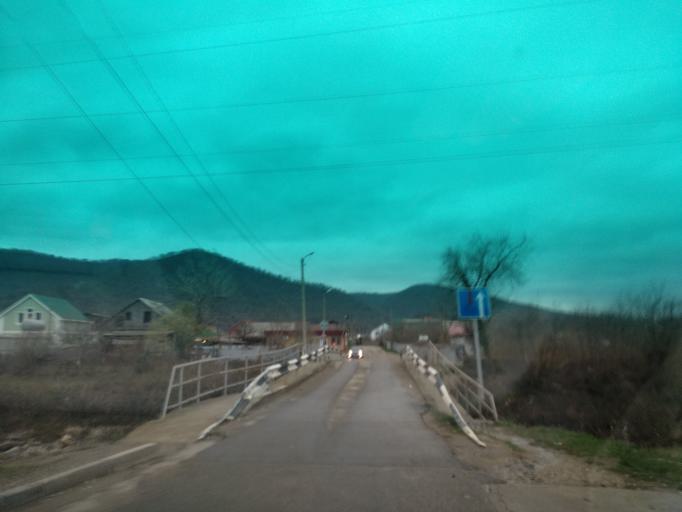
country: RU
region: Krasnodarskiy
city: Novomikhaylovskiy
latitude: 44.2592
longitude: 38.8617
